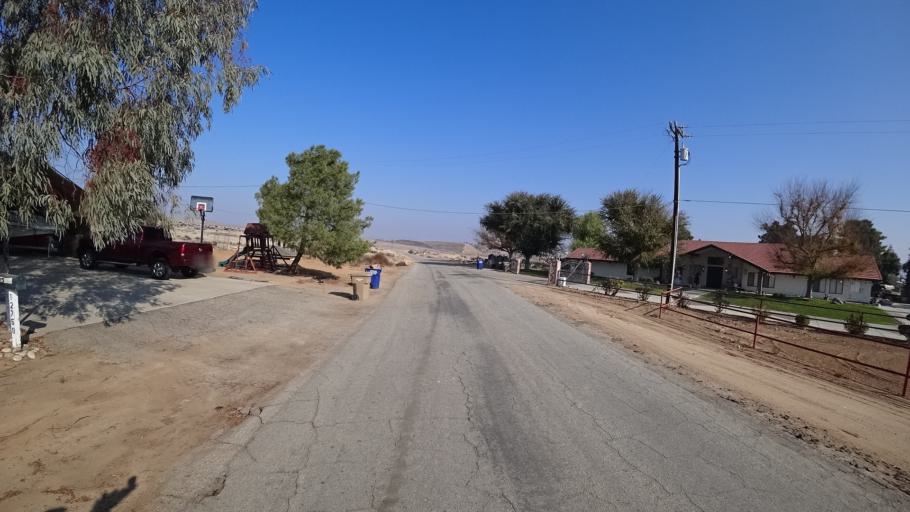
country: US
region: California
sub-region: Kern County
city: Oildale
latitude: 35.4087
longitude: -118.8656
